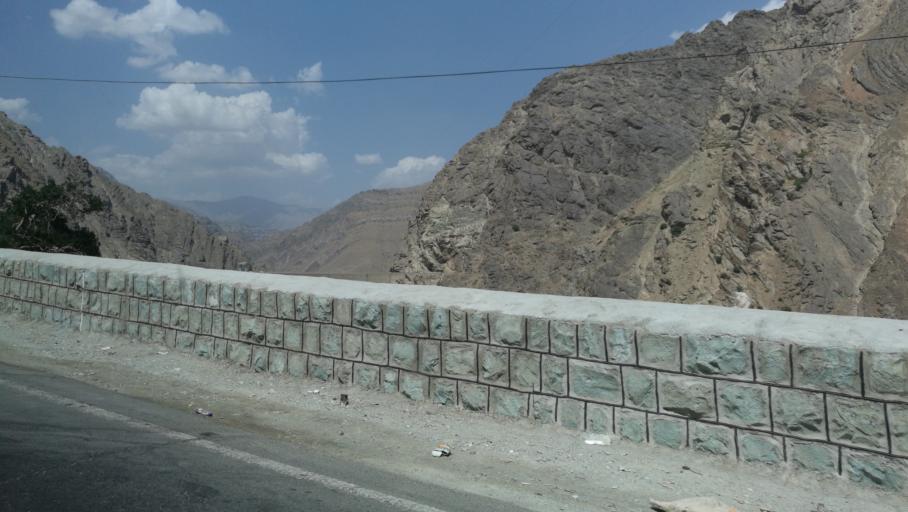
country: IR
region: Alborz
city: Karaj
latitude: 35.9511
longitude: 51.0870
